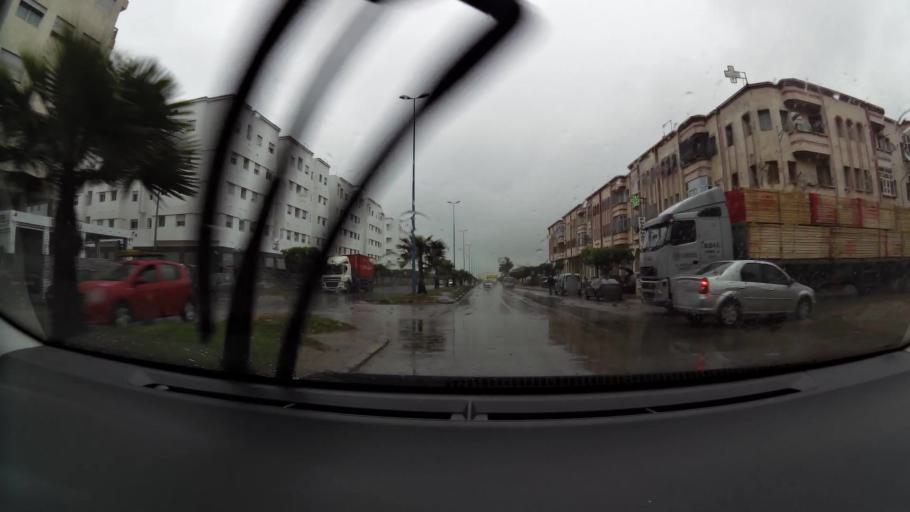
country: MA
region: Grand Casablanca
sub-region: Mediouna
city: Tit Mellil
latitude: 33.5952
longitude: -7.4988
